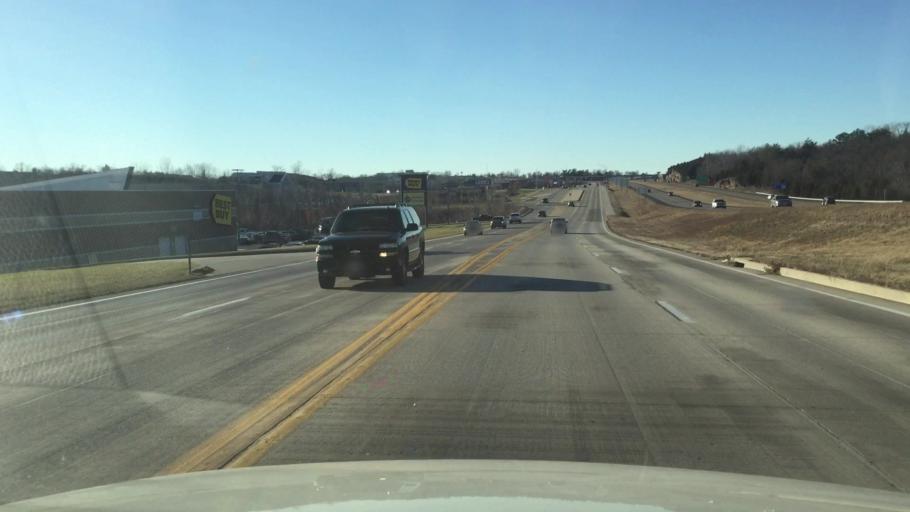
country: US
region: Missouri
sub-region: Cole County
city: Jefferson City
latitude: 38.5813
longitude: -92.2394
